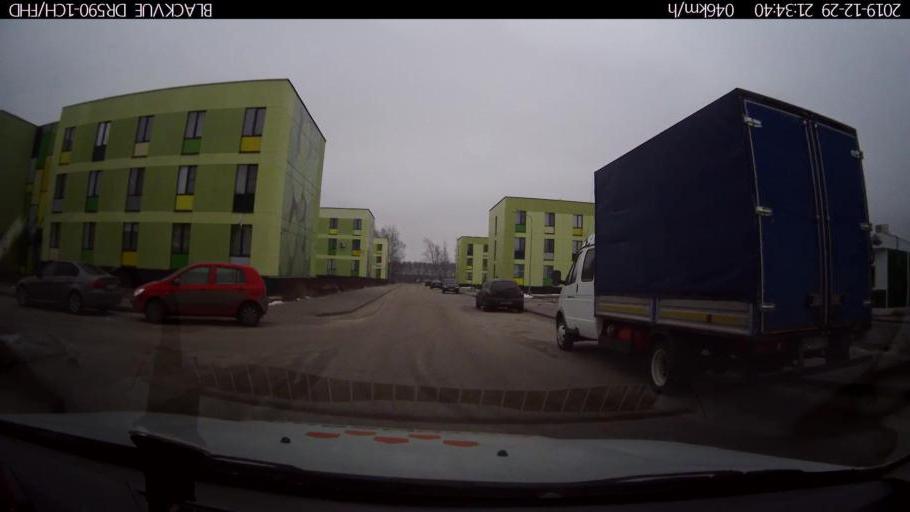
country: RU
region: Nizjnij Novgorod
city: Afonino
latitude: 56.2149
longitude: 44.0209
